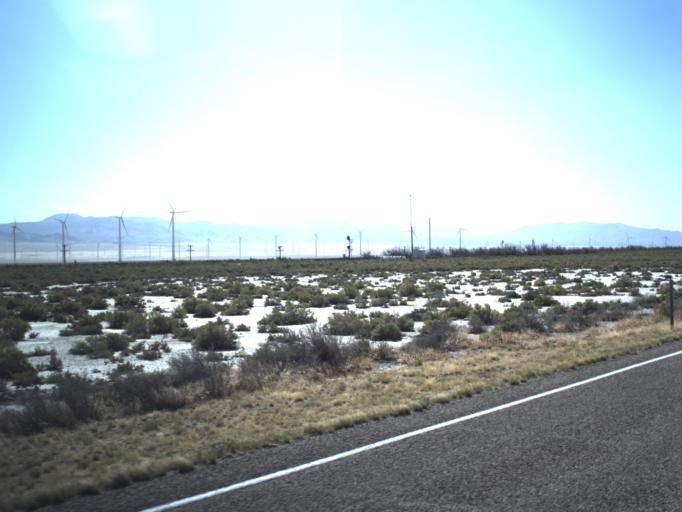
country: US
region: Utah
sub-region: Beaver County
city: Milford
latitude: 38.6031
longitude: -112.9870
